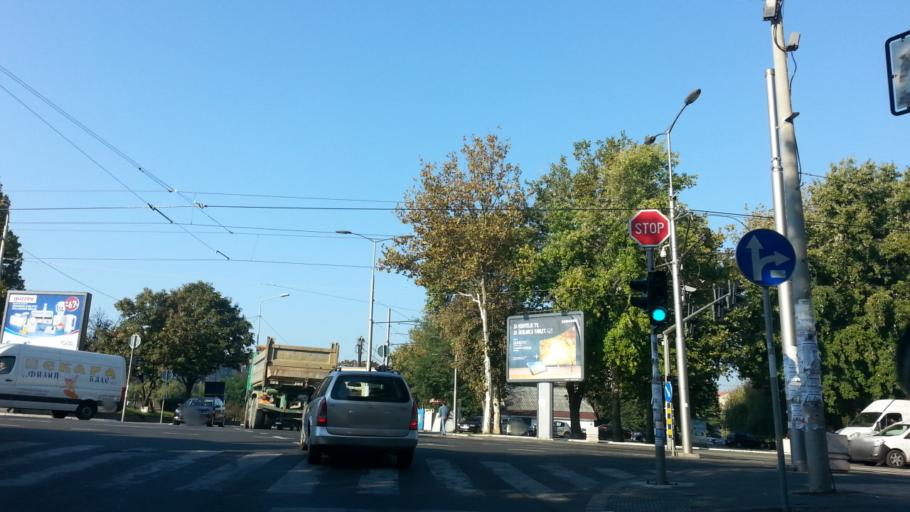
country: RS
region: Central Serbia
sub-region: Belgrade
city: Vozdovac
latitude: 44.7619
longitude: 20.4845
